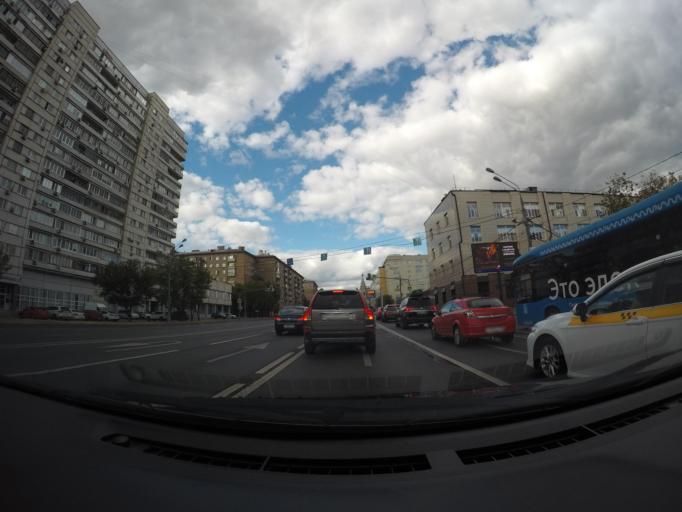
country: RU
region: Moscow
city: Mar'ina Roshcha
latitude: 55.7989
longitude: 37.5840
